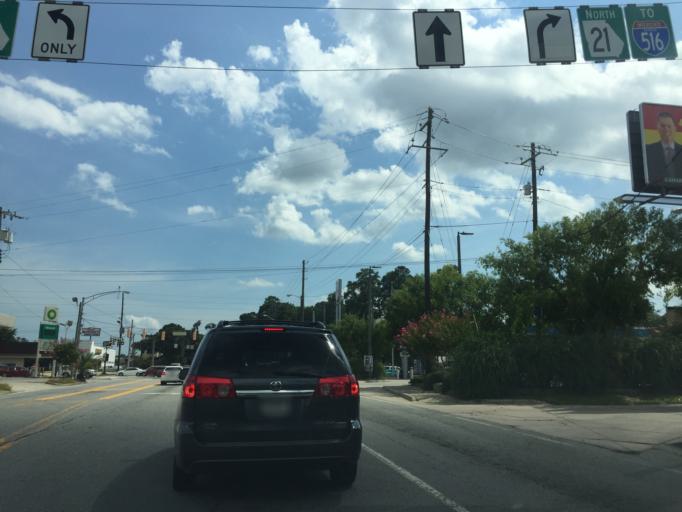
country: US
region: Georgia
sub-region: Chatham County
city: Savannah
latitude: 32.0298
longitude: -81.1106
